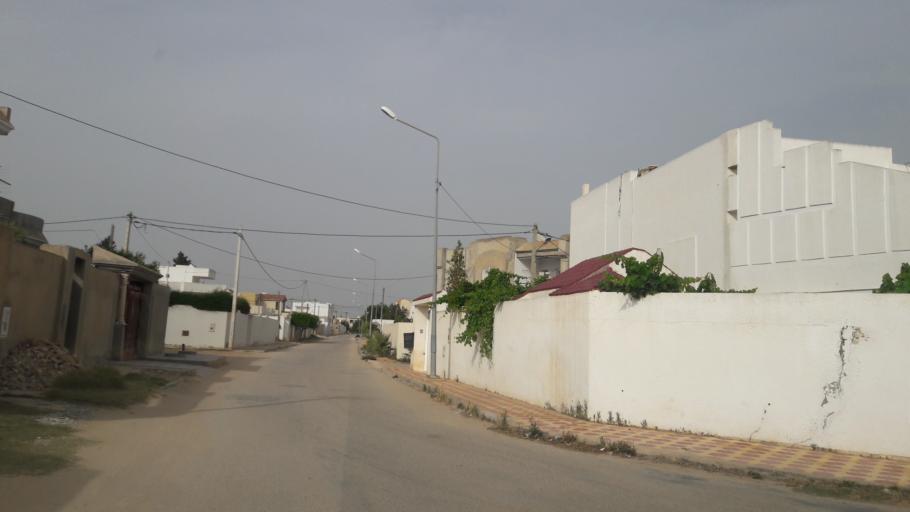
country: TN
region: Safaqis
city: Al Qarmadah
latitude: 34.7782
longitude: 10.7659
